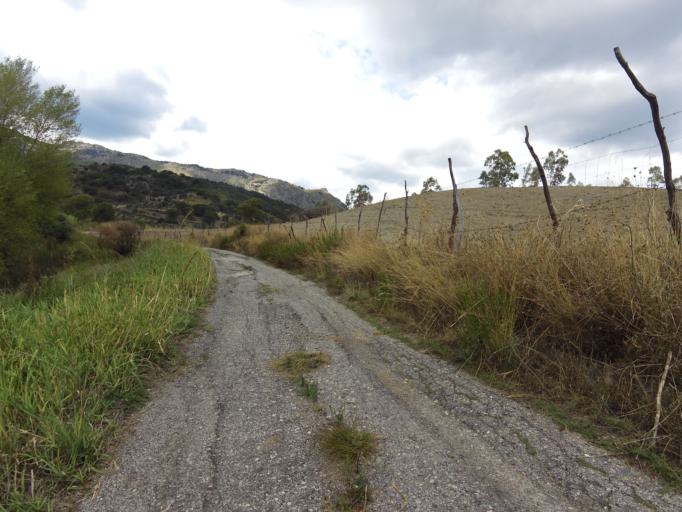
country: IT
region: Calabria
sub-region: Provincia di Reggio Calabria
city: Stilo
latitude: 38.4551
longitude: 16.4664
